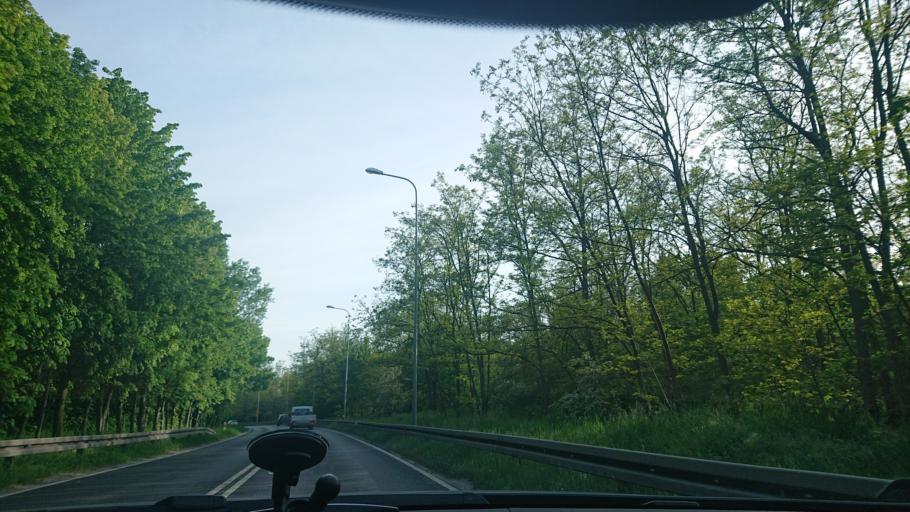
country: PL
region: Greater Poland Voivodeship
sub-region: Powiat gnieznienski
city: Gniezno
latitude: 52.5227
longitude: 17.5844
